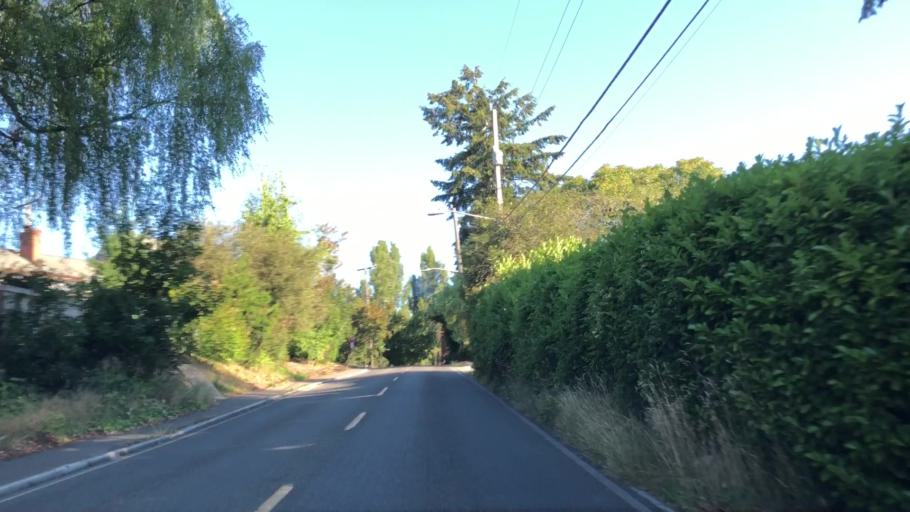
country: US
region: Washington
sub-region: King County
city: White Center
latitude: 47.5566
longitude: -122.3595
